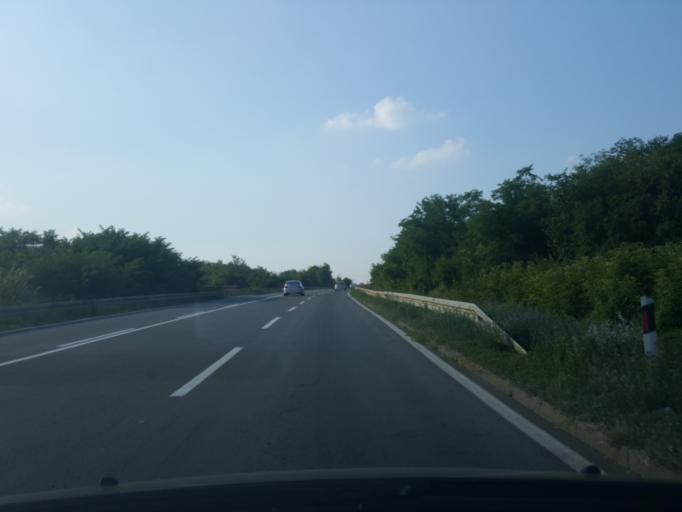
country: RS
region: Central Serbia
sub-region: Belgrade
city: Sopot
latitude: 44.5120
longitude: 20.6532
